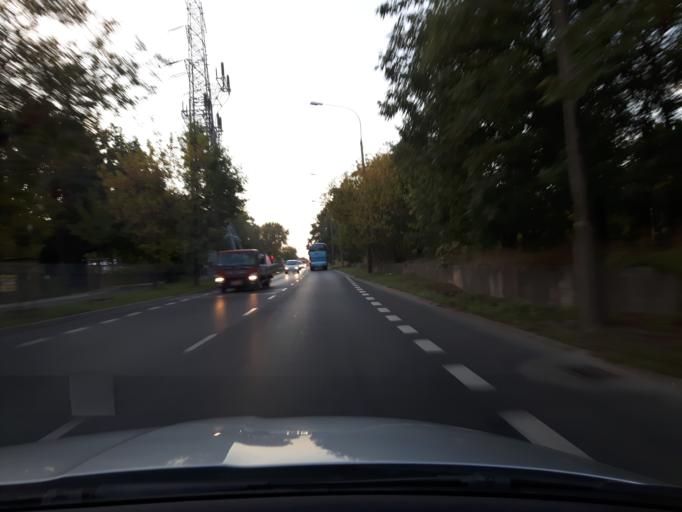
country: PL
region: Masovian Voivodeship
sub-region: Warszawa
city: Wawer
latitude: 52.2098
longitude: 21.1637
